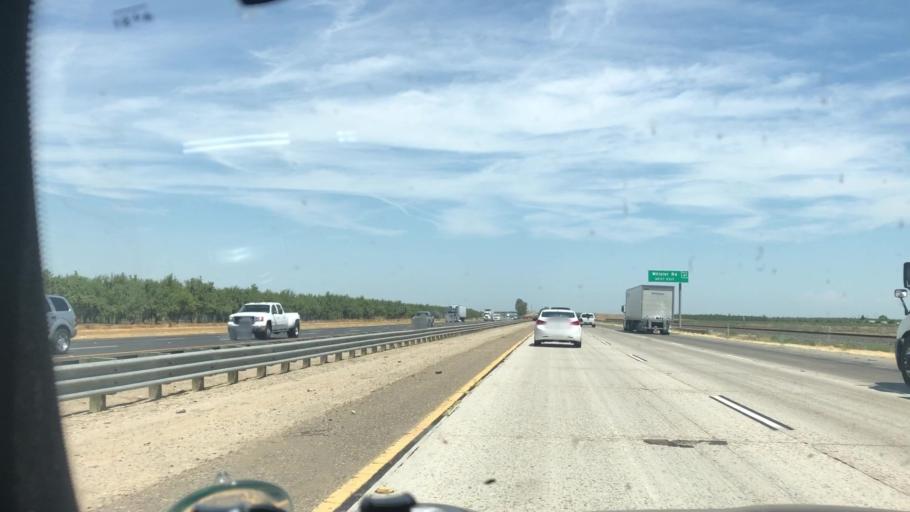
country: US
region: California
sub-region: Kern County
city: McFarland
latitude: 35.6346
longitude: -119.2170
